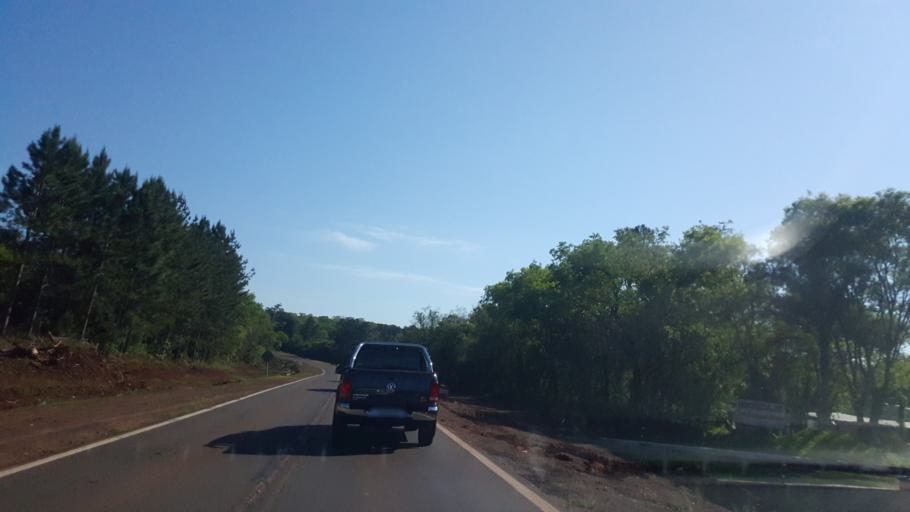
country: AR
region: Misiones
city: Santa Ana
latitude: -27.3656
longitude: -55.5587
